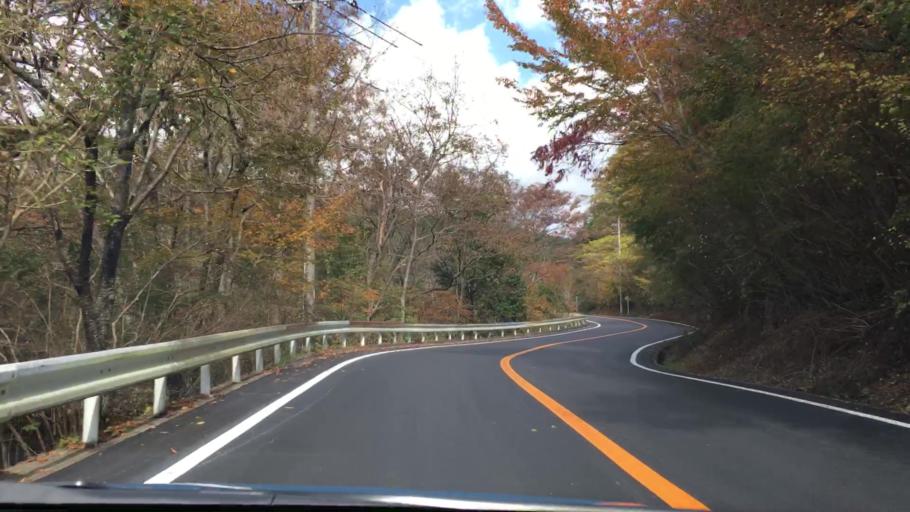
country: JP
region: Shizuoka
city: Gotemba
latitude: 35.3831
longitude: 138.9430
